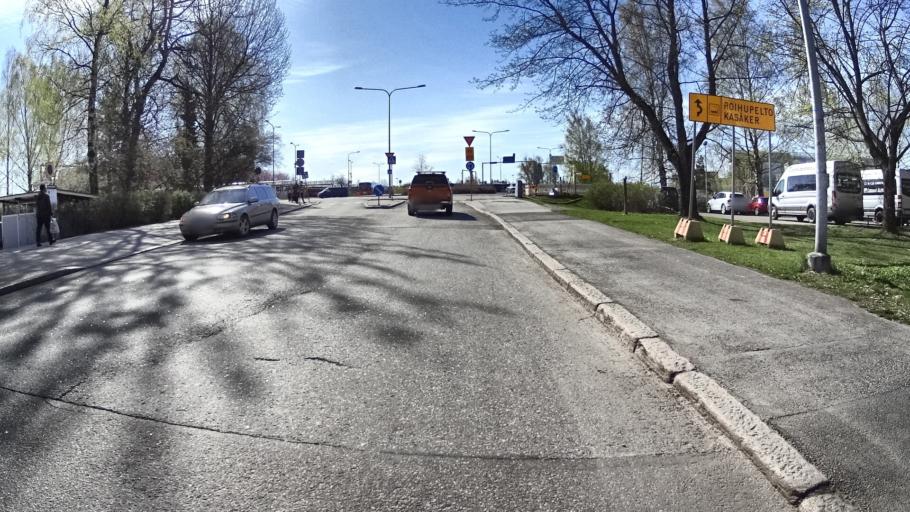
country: FI
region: Uusimaa
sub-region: Helsinki
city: Vantaa
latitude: 60.2105
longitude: 25.0745
